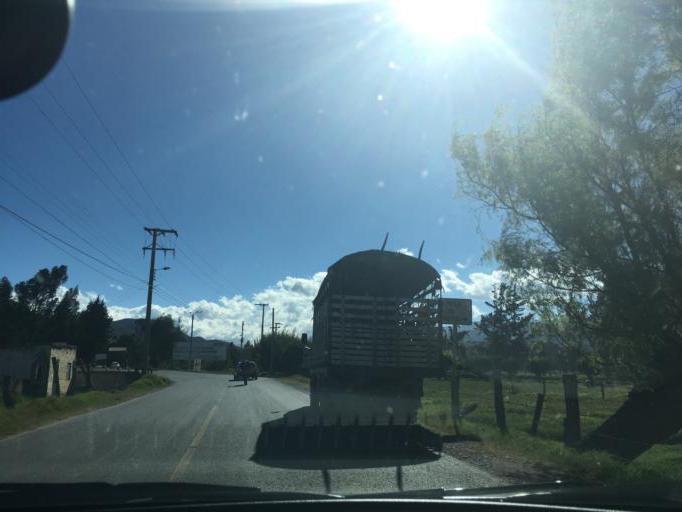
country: CO
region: Boyaca
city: Firavitoba
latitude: 5.6453
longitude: -72.9891
